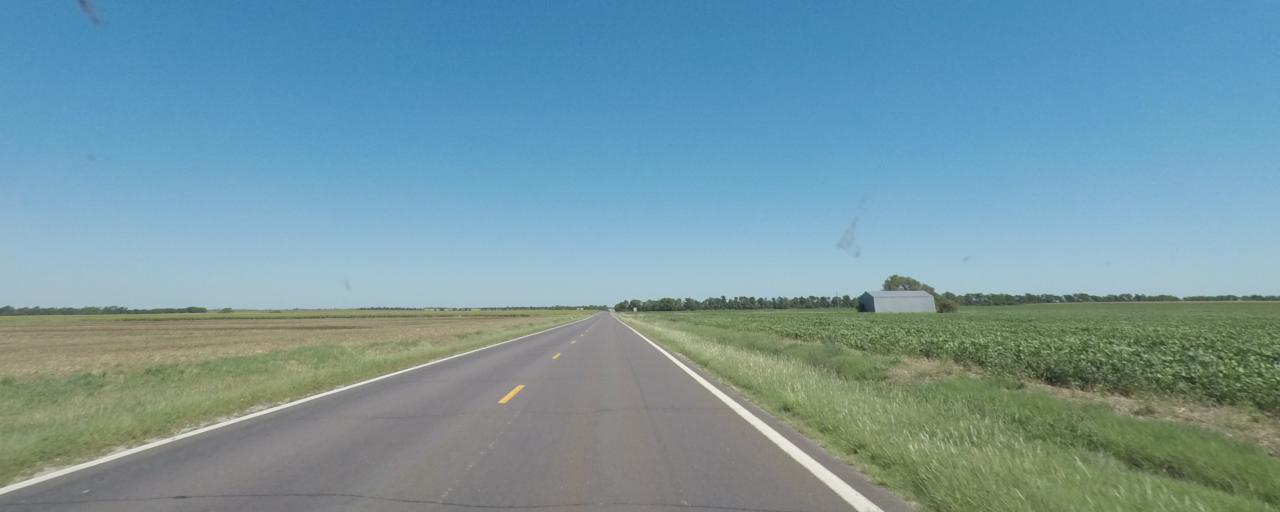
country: US
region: Kansas
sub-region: Sumner County
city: Wellington
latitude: 37.1750
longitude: -97.4019
